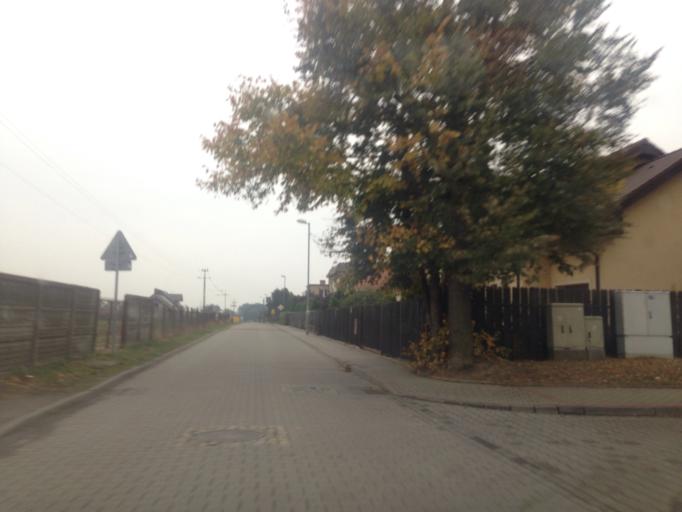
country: PL
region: Greater Poland Voivodeship
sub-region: Powiat poznanski
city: Swarzedz
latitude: 52.3439
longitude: 17.0737
